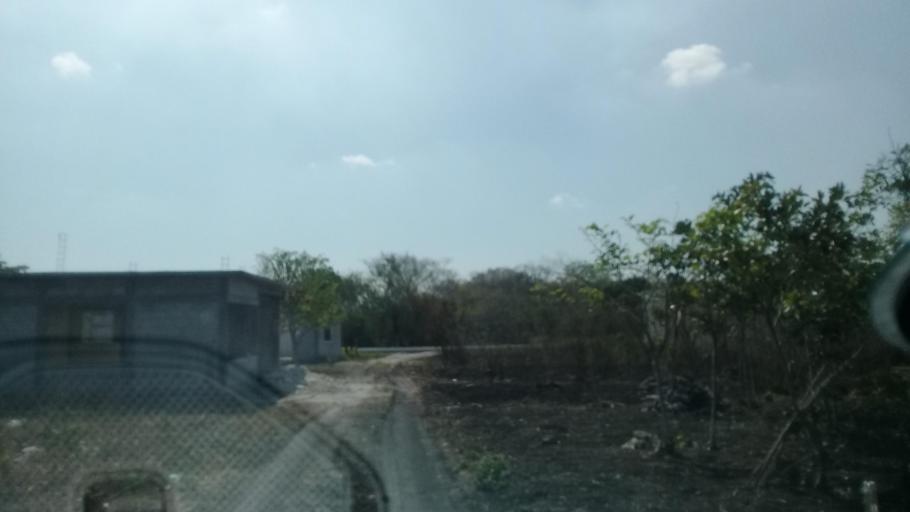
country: MX
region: Veracruz
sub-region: Emiliano Zapata
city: Plan del Rio
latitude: 19.4022
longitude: -96.6154
